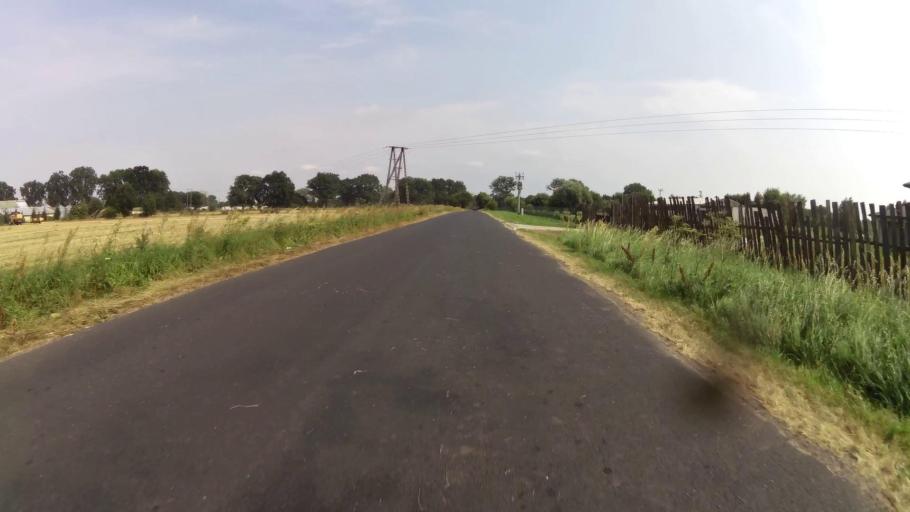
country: PL
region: West Pomeranian Voivodeship
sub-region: Powiat pyrzycki
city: Lipiany
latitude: 52.9672
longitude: 15.0015
